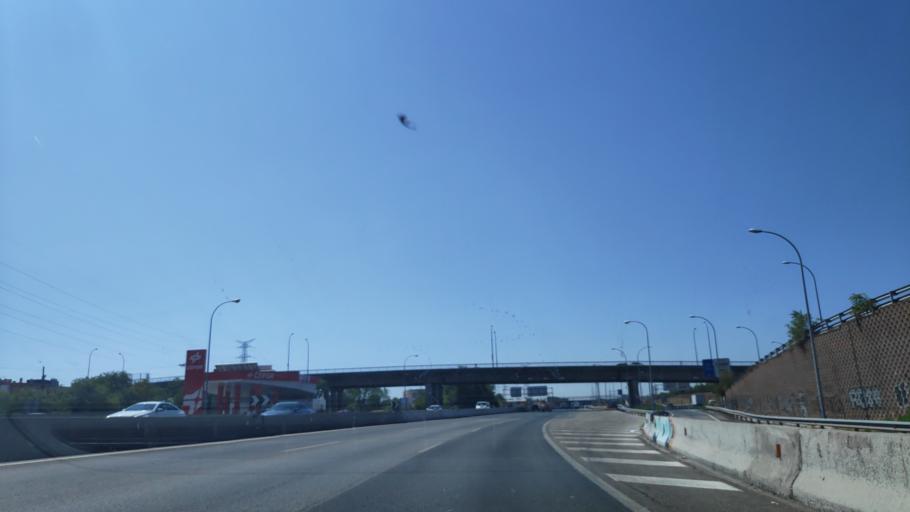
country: ES
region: Madrid
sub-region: Provincia de Madrid
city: Getafe
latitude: 40.3283
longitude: -3.7258
